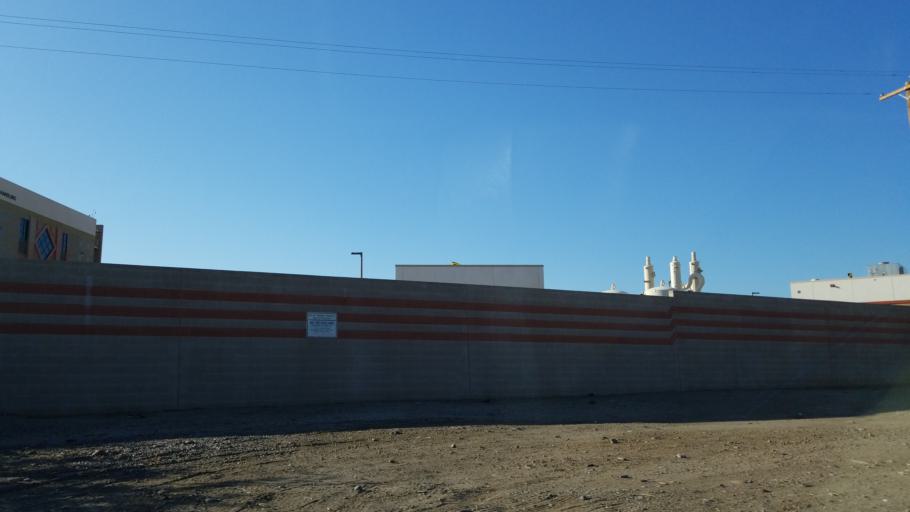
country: US
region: Arizona
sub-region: Maricopa County
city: Phoenix
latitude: 33.4224
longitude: -112.1098
